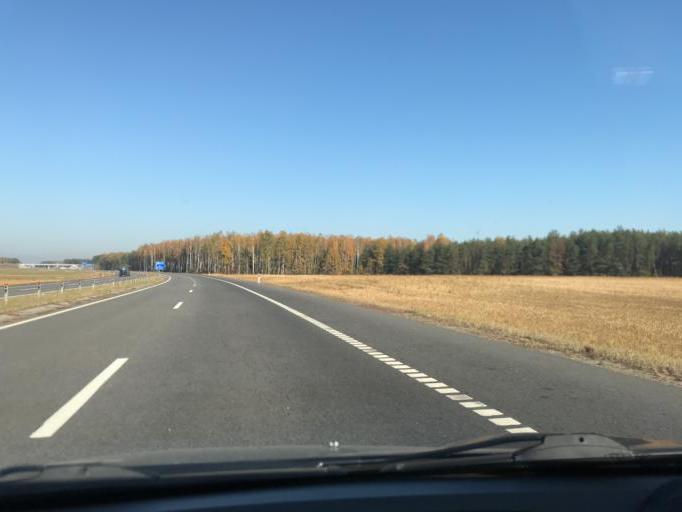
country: BY
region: Mogilev
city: Babruysk
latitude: 53.1314
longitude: 29.3663
